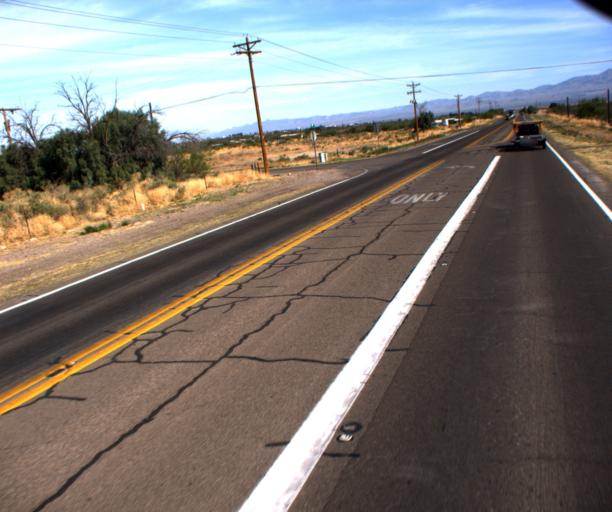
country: US
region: Arizona
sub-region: Graham County
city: Cactus Flat
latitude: 32.7510
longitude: -109.7163
